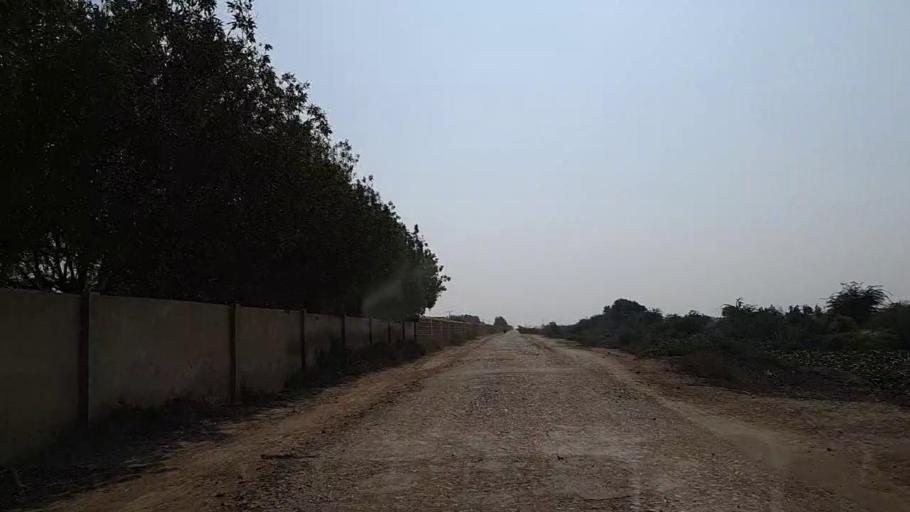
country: PK
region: Sindh
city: Thatta
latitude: 24.7260
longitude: 67.7684
